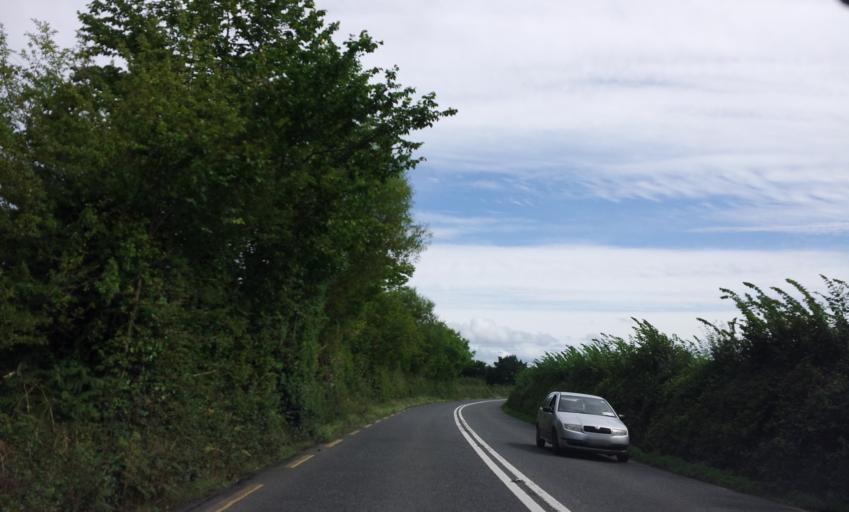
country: IE
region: Munster
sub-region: Ciarrai
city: Killorglin
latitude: 52.1010
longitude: -9.7137
